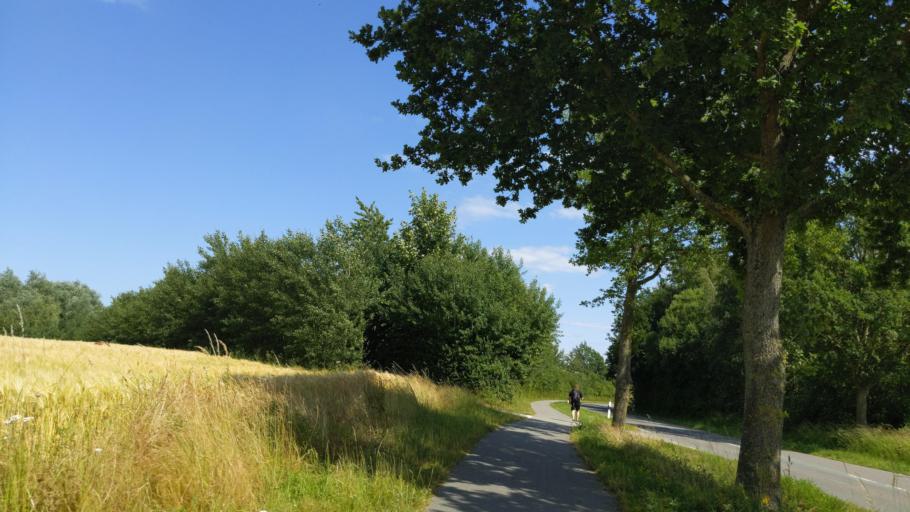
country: DE
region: Schleswig-Holstein
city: Gromitz
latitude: 54.1536
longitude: 10.9422
